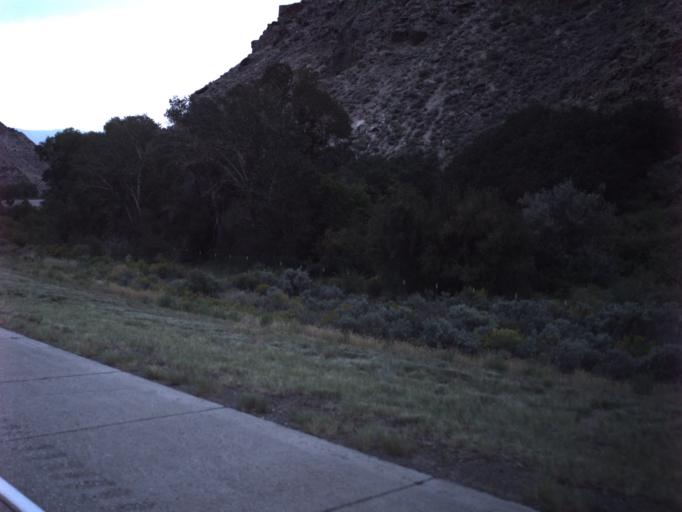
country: US
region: Utah
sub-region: Sevier County
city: Monroe
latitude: 38.5779
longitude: -112.3297
